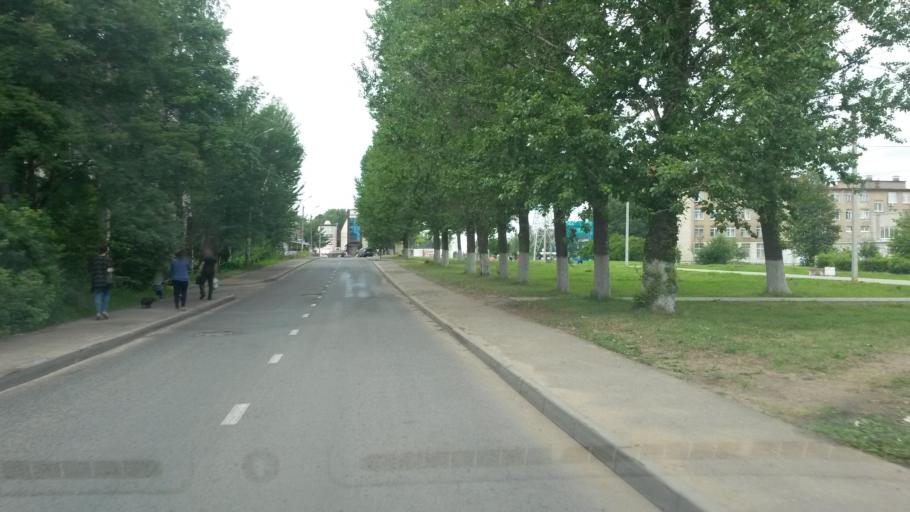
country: RU
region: Jaroslavl
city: Yaroslavl
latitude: 57.5844
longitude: 39.8589
